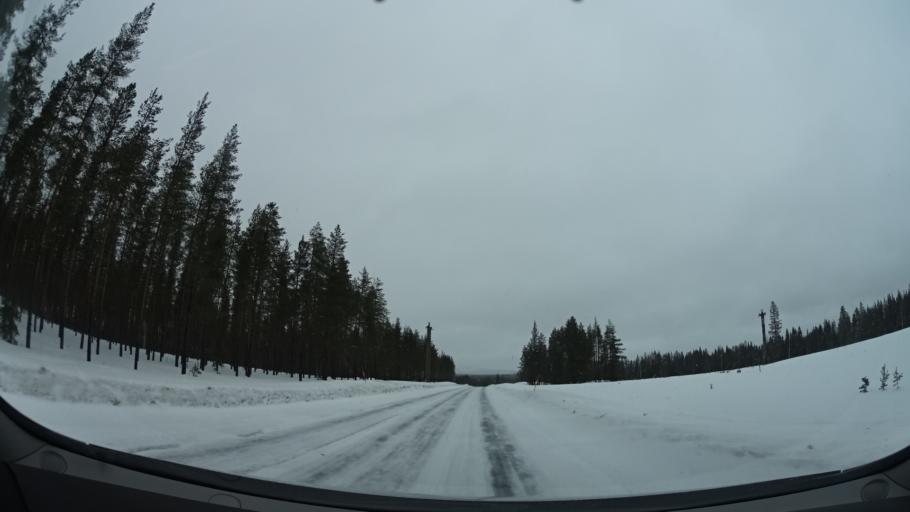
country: SE
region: Vaesterbotten
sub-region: Mala Kommun
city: Mala
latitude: 65.1277
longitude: 18.8712
